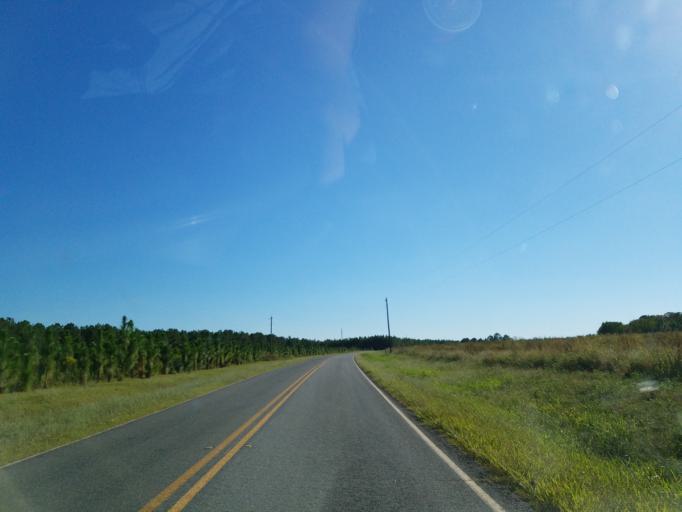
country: US
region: Georgia
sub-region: Dooly County
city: Unadilla
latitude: 32.2221
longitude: -83.8839
